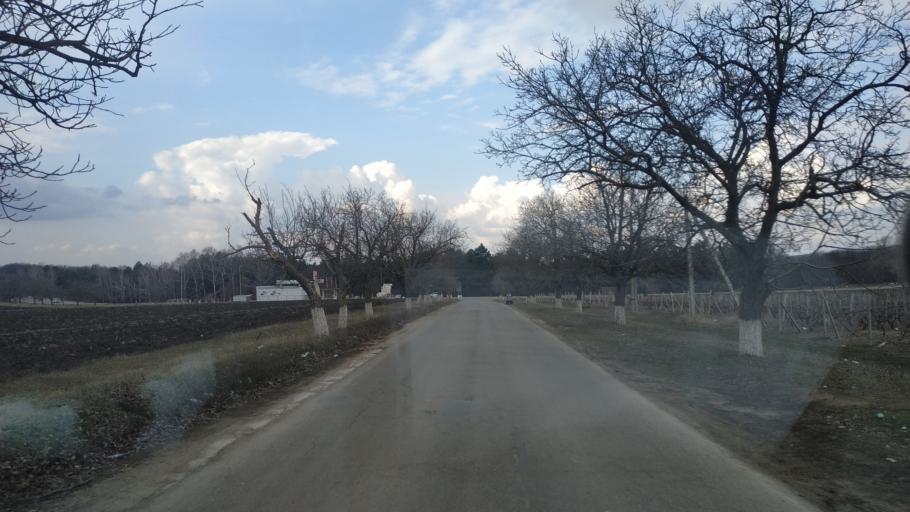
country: MD
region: Anenii Noi
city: Anenii Noi
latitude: 46.8548
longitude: 29.3491
